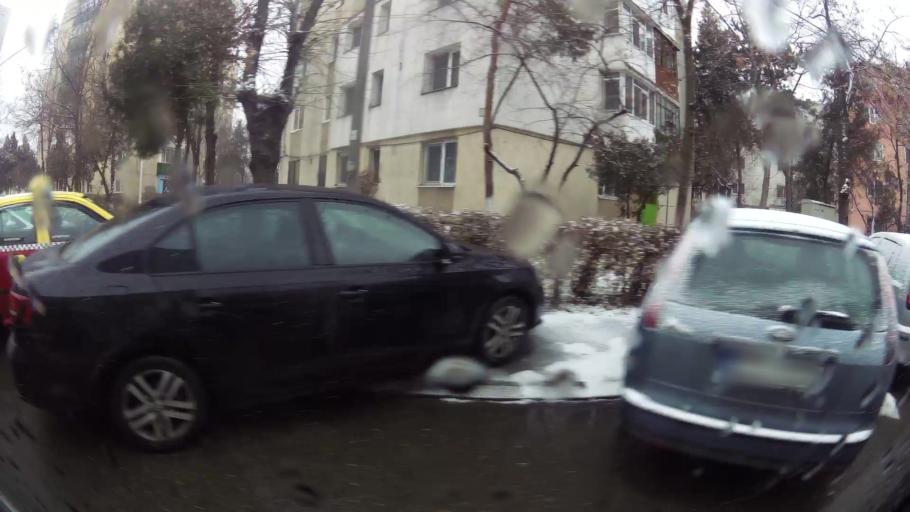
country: RO
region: Prahova
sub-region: Comuna Targsoru Vechi
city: Strejnicu
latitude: 44.9352
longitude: 25.9829
